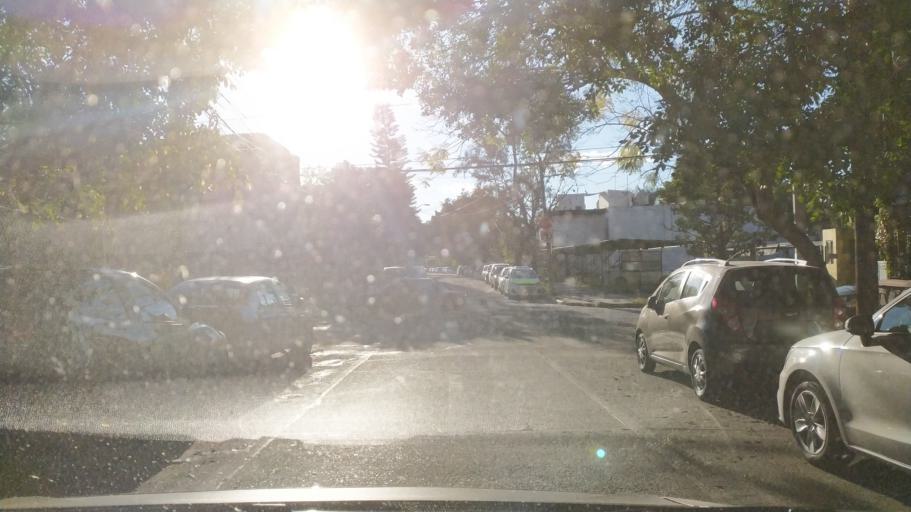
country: MX
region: Jalisco
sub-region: Zapopan
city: Zapopan
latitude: 20.7019
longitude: -103.3781
